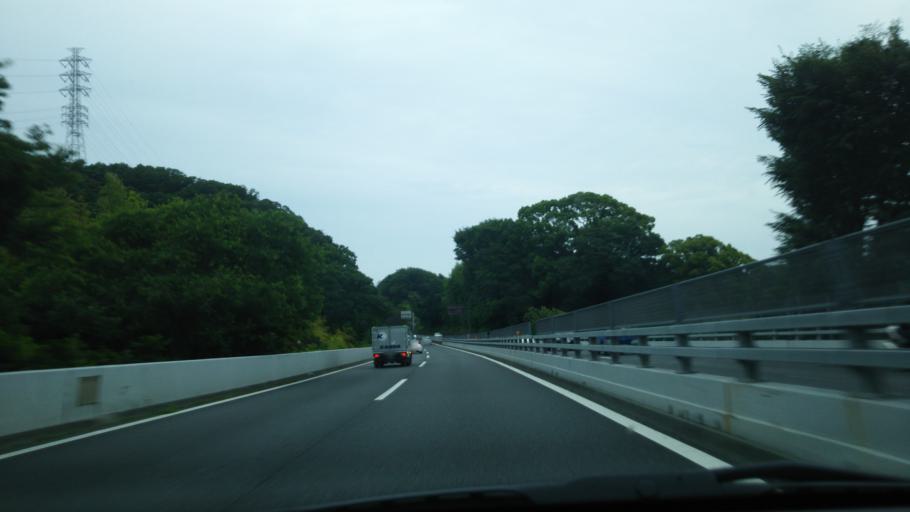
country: JP
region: Kanagawa
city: Ninomiya
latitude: 35.3207
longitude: 139.2757
